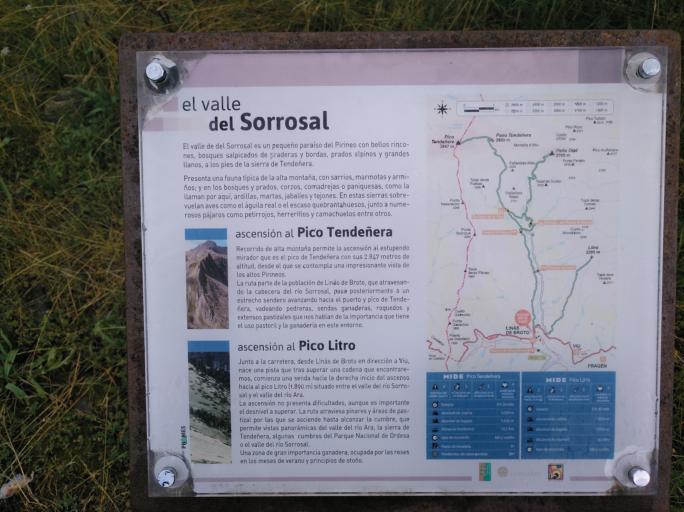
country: ES
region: Aragon
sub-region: Provincia de Huesca
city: Broto
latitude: 42.6236
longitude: -0.1687
